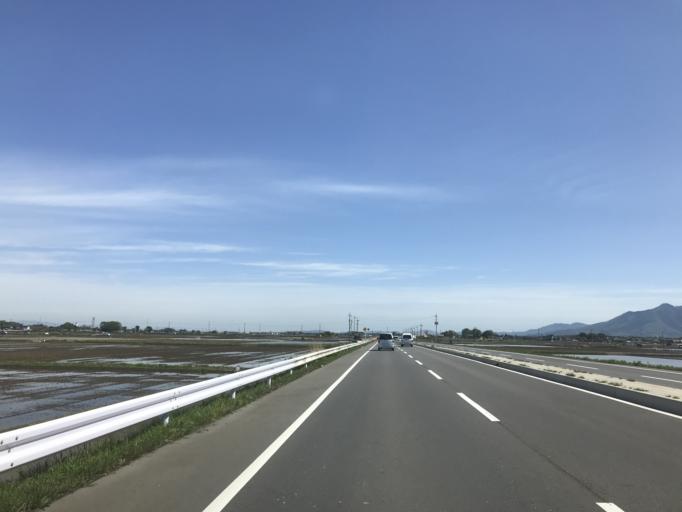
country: JP
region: Ibaraki
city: Ishige
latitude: 36.1358
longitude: 139.9853
